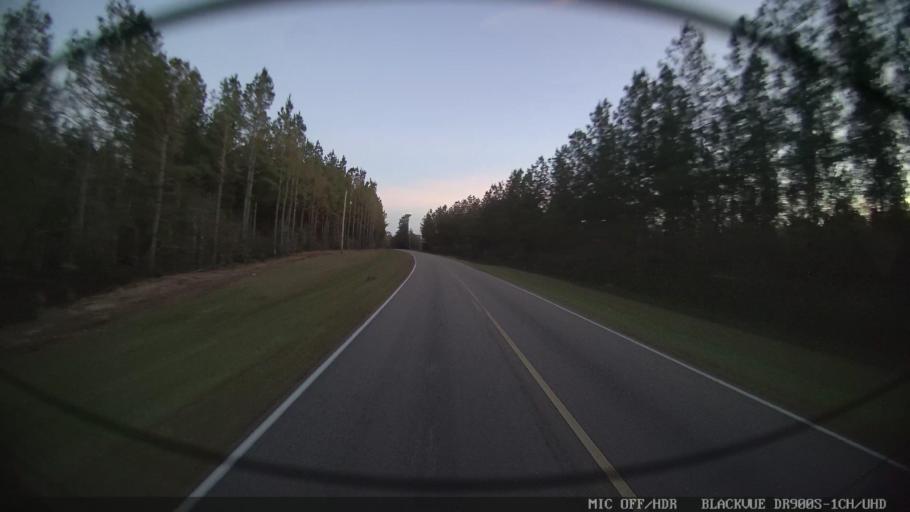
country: US
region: Mississippi
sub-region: Perry County
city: New Augusta
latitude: 31.0963
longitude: -89.1914
